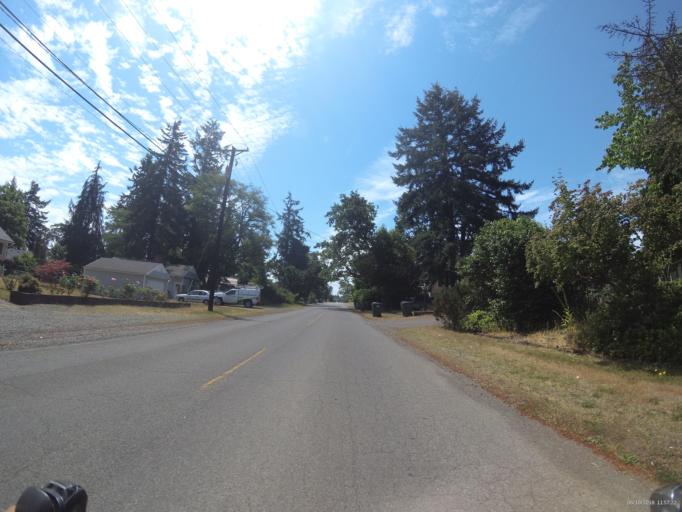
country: US
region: Washington
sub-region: Pierce County
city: Lakewood
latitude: 47.1759
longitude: -122.5218
